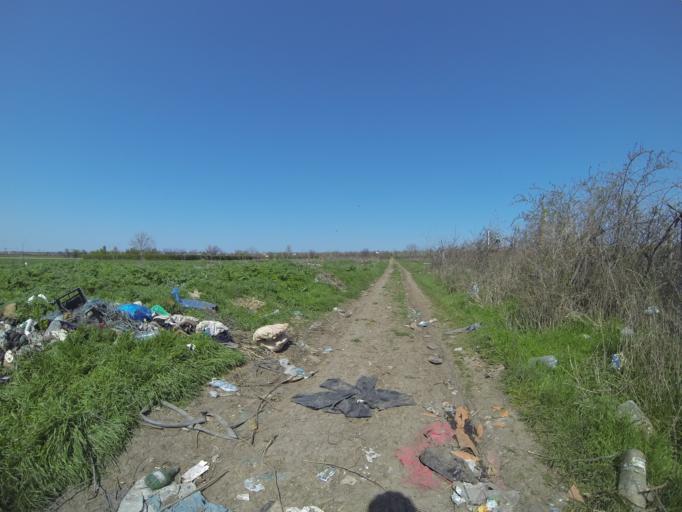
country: RO
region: Dolj
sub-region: Comuna Segarcea
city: Segarcea
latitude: 44.0939
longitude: 23.7289
